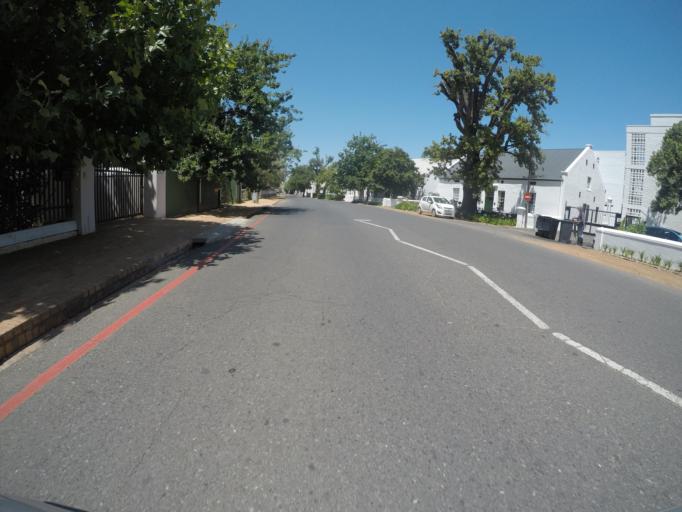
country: ZA
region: Western Cape
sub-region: Cape Winelands District Municipality
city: Stellenbosch
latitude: -33.9380
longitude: 18.8550
